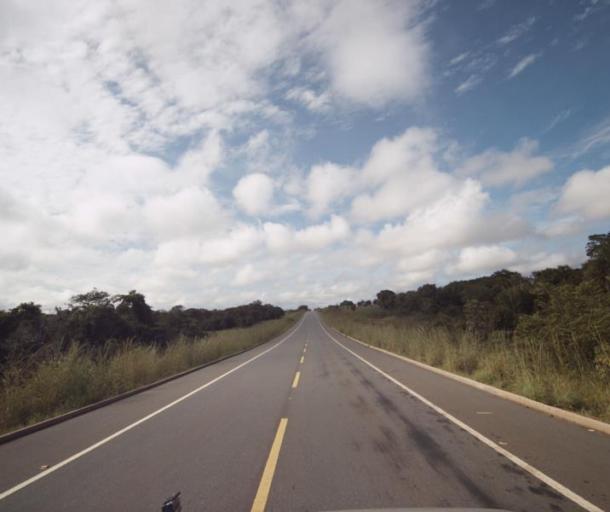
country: BR
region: Goias
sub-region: Barro Alto
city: Barro Alto
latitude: -15.2332
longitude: -48.6932
